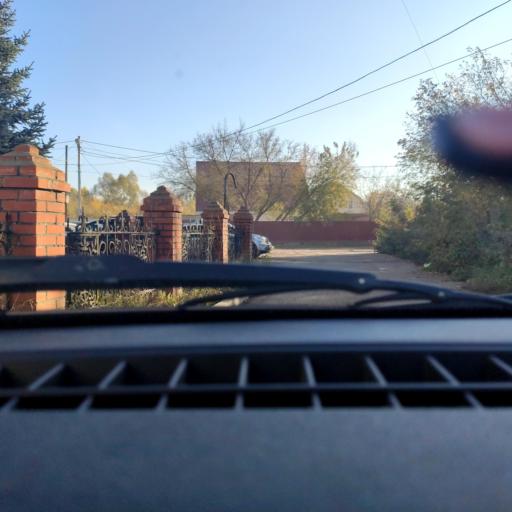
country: RU
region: Bashkortostan
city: Ufa
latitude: 54.7997
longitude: 56.1565
